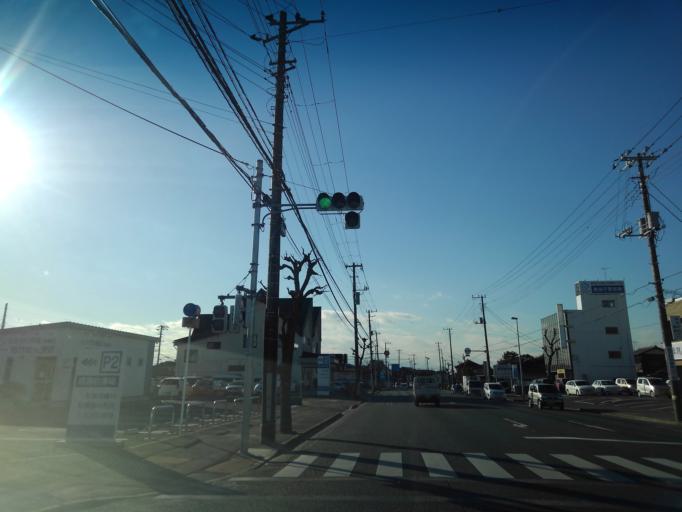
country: JP
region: Chiba
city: Kimitsu
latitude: 35.3292
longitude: 139.8997
